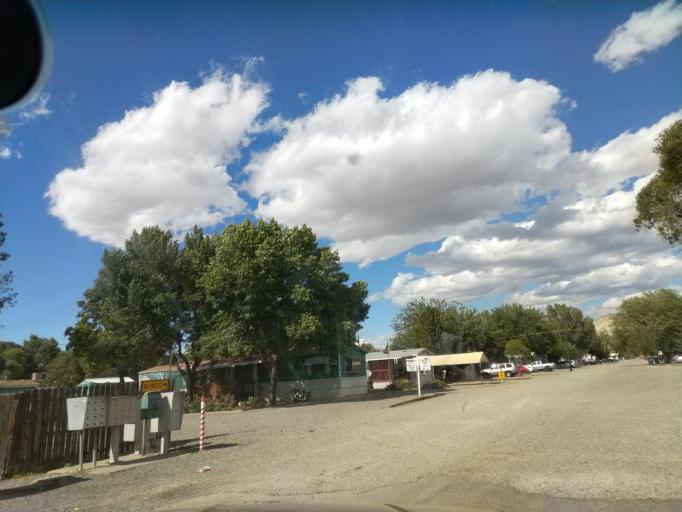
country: US
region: Colorado
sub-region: Mesa County
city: Clifton
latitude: 39.0923
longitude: -108.4553
